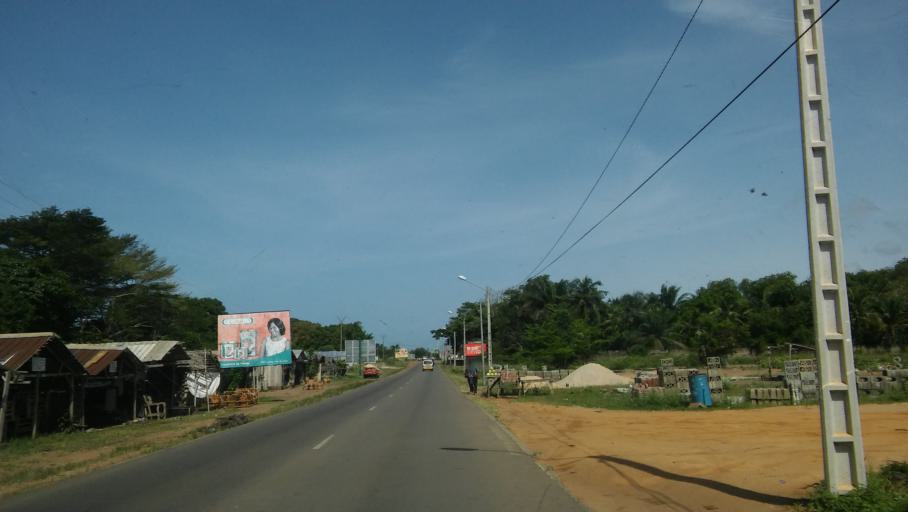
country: CI
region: Sud-Comoe
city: Grand-Bassam
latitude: 5.2109
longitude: -3.7677
